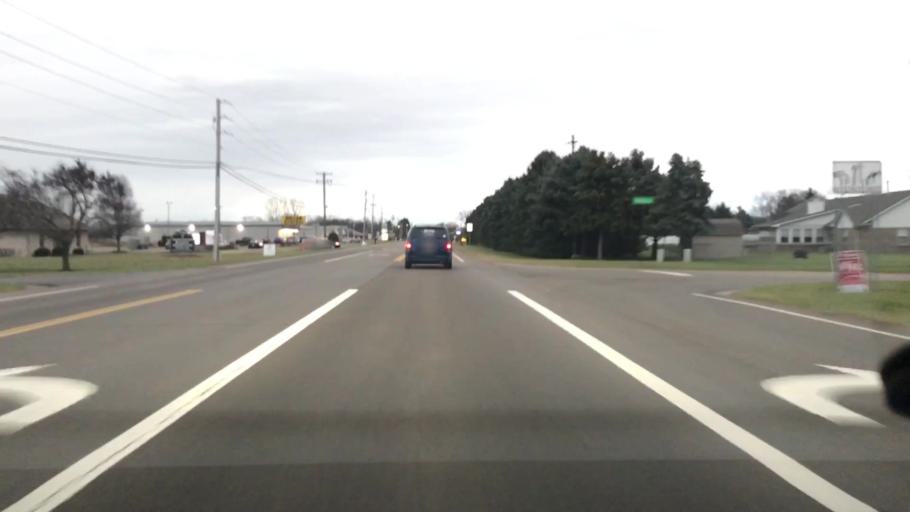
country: US
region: Ohio
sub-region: Clark County
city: Holiday Valley
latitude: 39.8633
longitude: -83.9623
